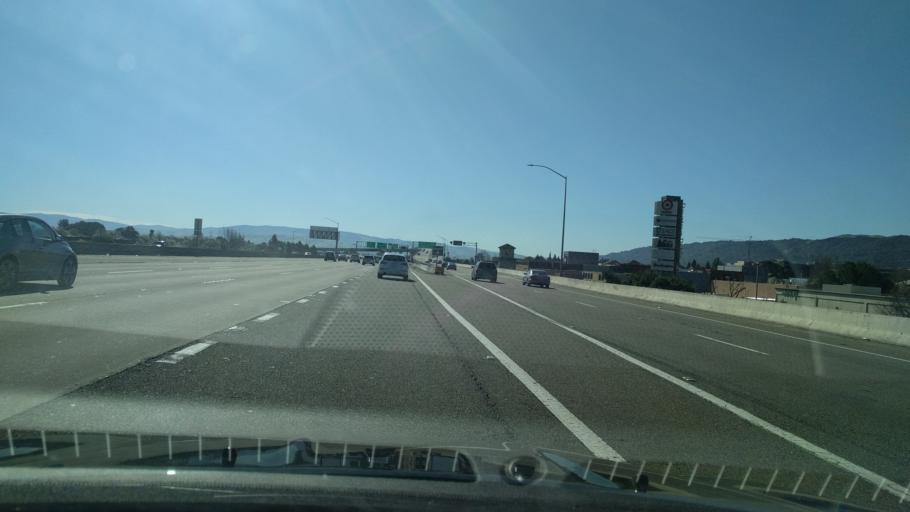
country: US
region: California
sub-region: Alameda County
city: Dublin
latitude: 37.7091
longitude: -121.9286
